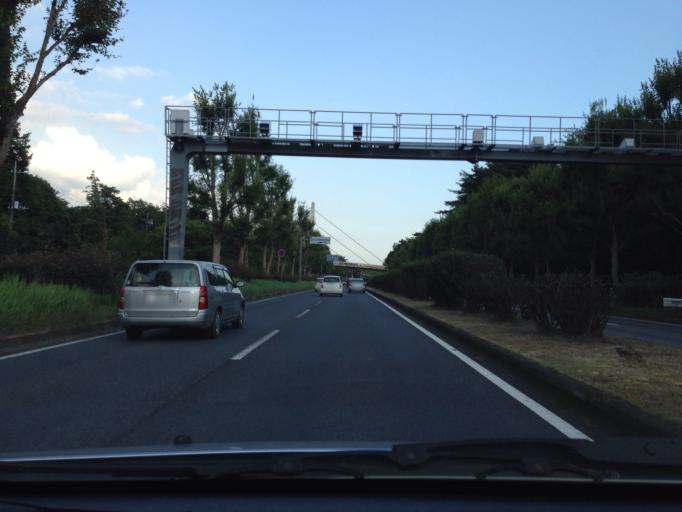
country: JP
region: Ibaraki
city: Naka
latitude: 36.0628
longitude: 140.1389
